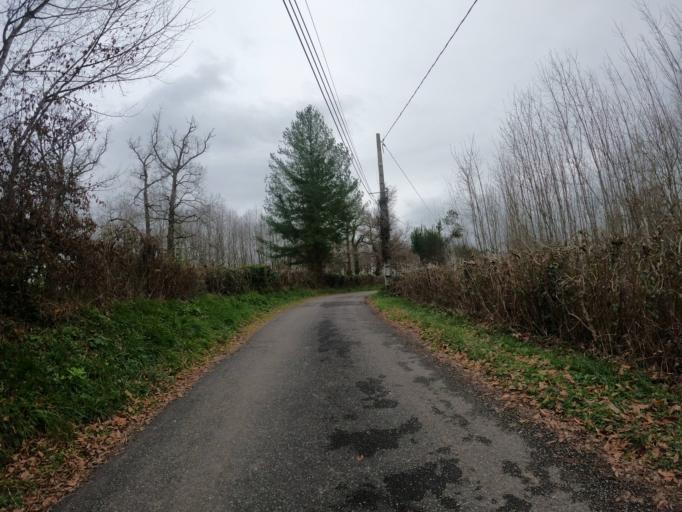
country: FR
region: Aquitaine
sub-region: Departement des Pyrenees-Atlantiques
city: Mazeres-Lezons
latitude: 43.2639
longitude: -0.3502
